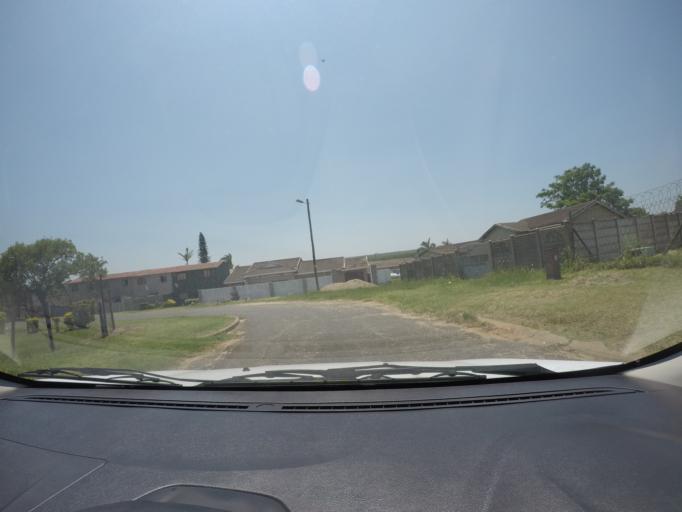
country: ZA
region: KwaZulu-Natal
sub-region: uThungulu District Municipality
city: eSikhawini
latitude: -28.8843
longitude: 31.8884
